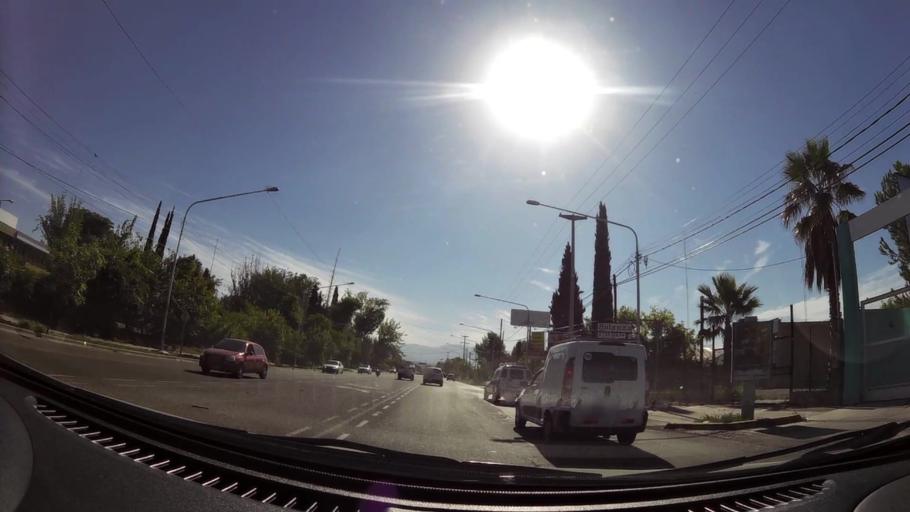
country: AR
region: Mendoza
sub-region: Departamento de Godoy Cruz
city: Godoy Cruz
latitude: -32.9283
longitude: -68.8146
